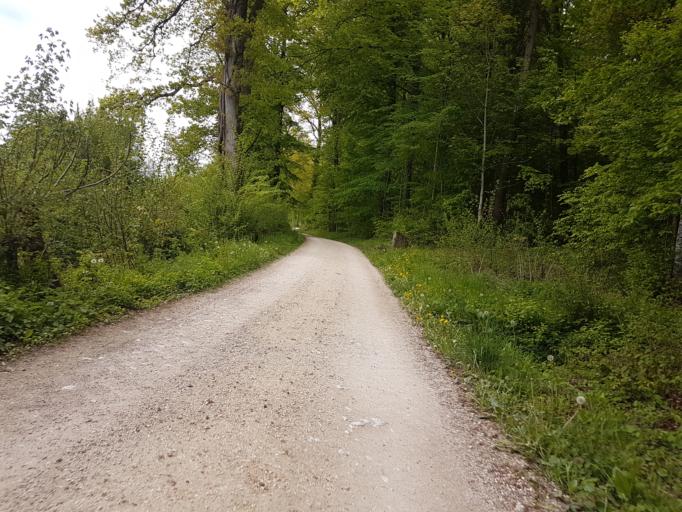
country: CH
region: Solothurn
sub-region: Bezirk Solothurn
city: Solothurn
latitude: 47.1918
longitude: 7.5183
